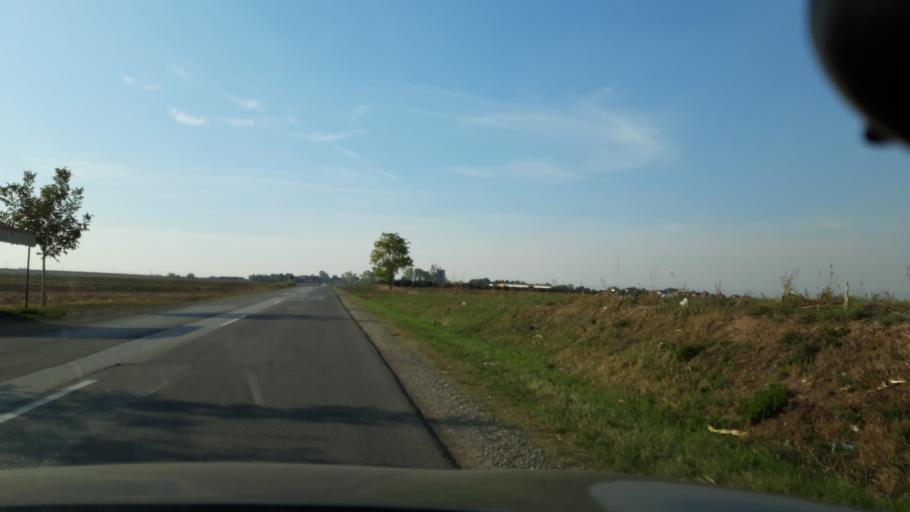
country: RS
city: Putinci
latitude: 44.9979
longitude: 19.9505
